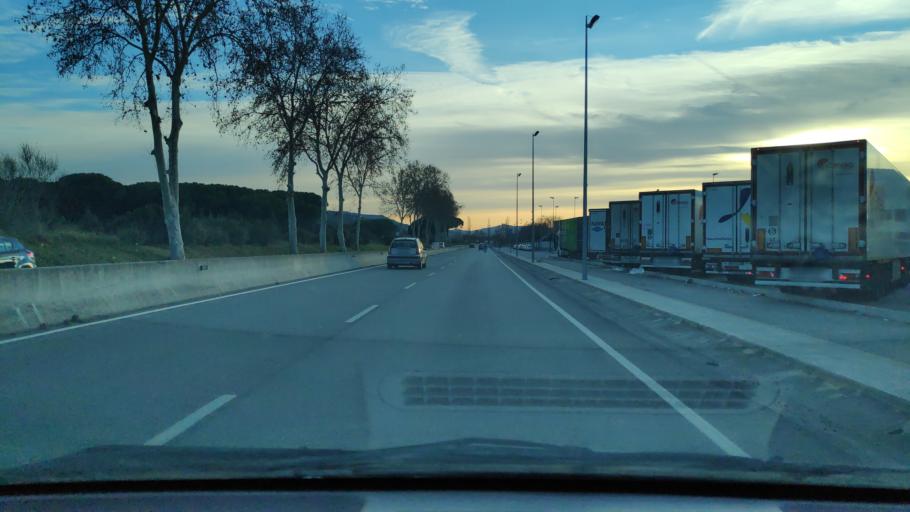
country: ES
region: Catalonia
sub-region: Provincia de Barcelona
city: Montmelo
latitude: 41.5686
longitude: 2.2677
